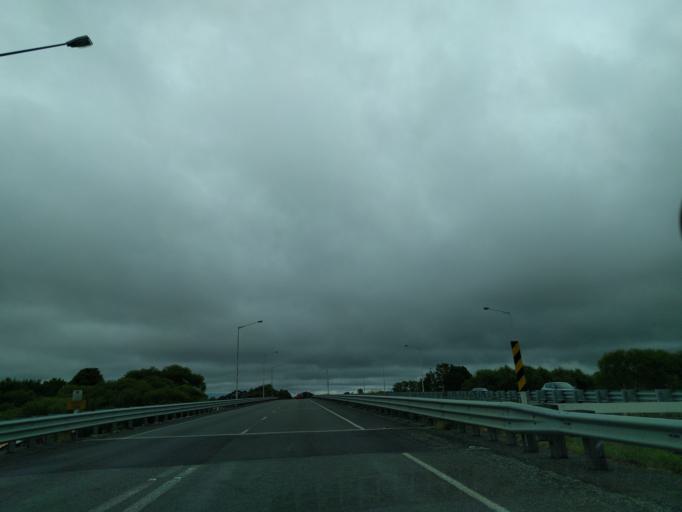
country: NZ
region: Canterbury
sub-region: Waimakariri District
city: Kaiapoi
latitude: -43.3793
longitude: 172.6446
